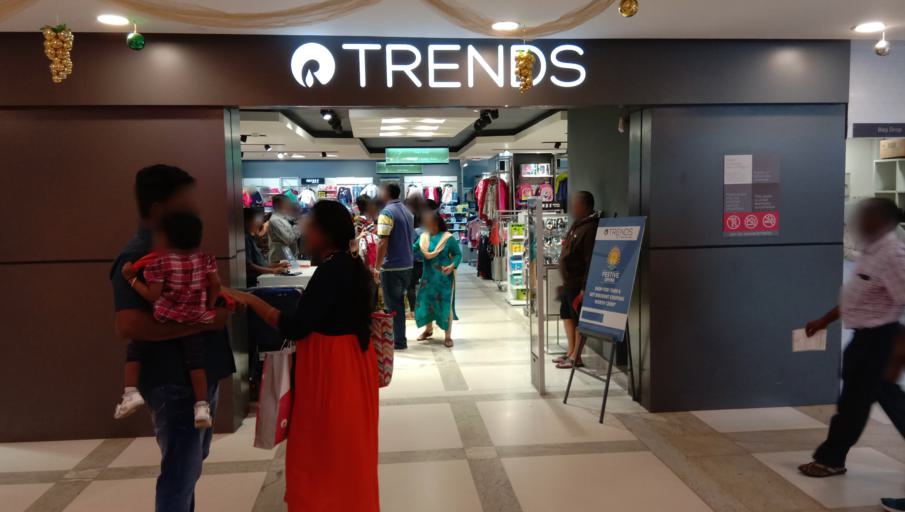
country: IN
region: Karnataka
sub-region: Bangalore Urban
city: Bangalore
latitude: 12.9165
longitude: 77.6714
